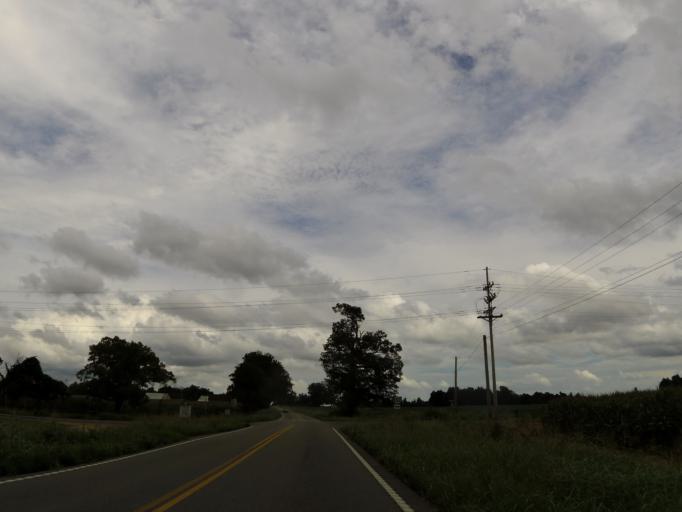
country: US
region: Kentucky
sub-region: Ballard County
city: La Center
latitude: 36.9888
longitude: -88.9535
